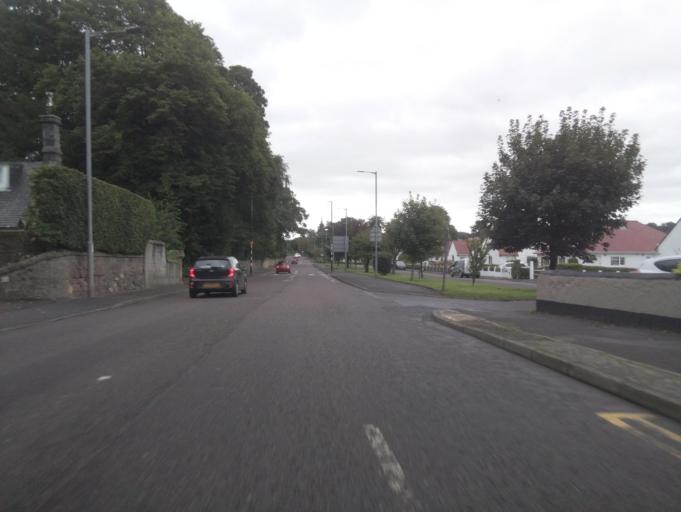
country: GB
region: Scotland
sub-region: Clackmannanshire
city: Tillicoultry
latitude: 56.1530
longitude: -3.7388
